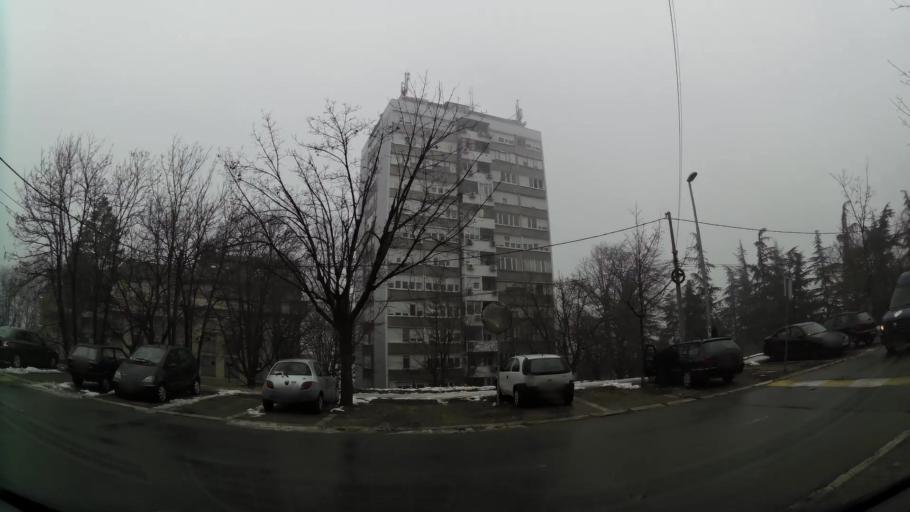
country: RS
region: Central Serbia
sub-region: Belgrade
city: Cukarica
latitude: 44.7758
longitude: 20.4197
